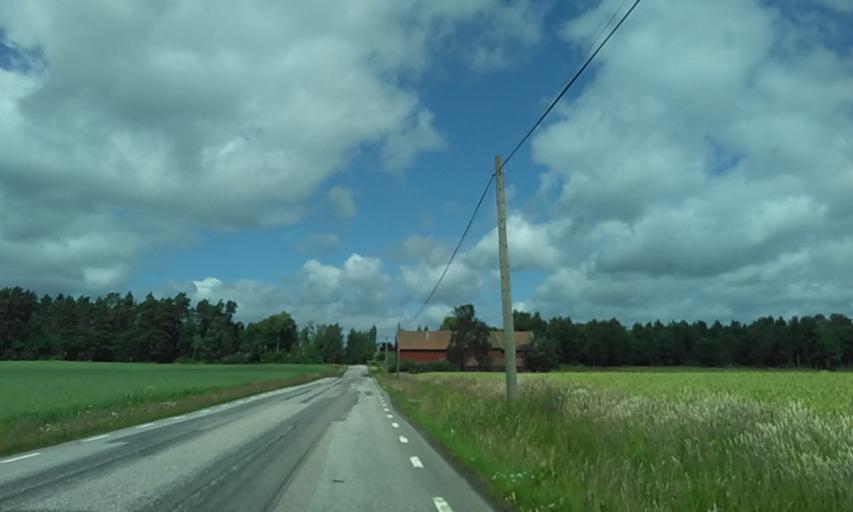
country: SE
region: Vaestra Goetaland
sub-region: Vargarda Kommun
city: Vargarda
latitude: 58.1196
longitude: 12.7881
